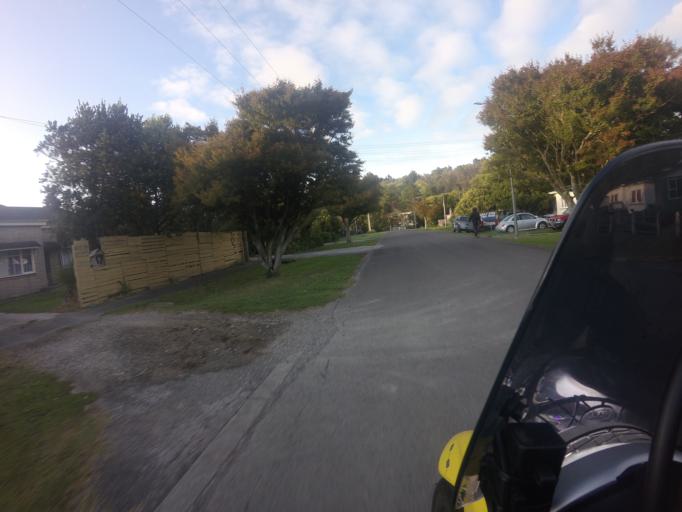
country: NZ
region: Gisborne
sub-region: Gisborne District
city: Gisborne
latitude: -38.6714
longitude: 178.0328
